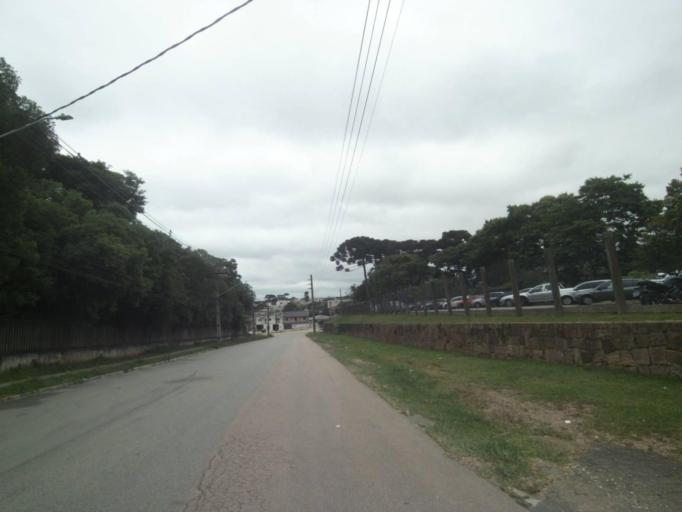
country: BR
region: Parana
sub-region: Araucaria
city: Araucaria
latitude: -25.5589
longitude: -49.3105
